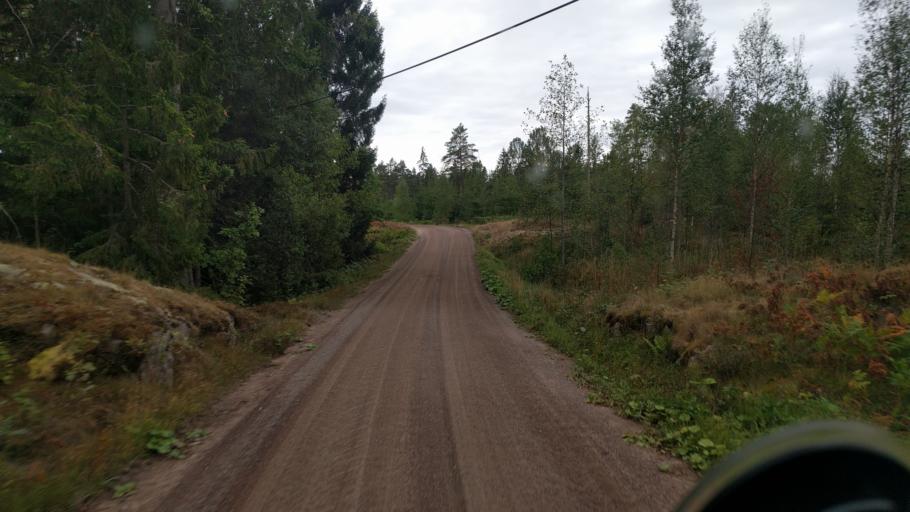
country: SE
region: Kalmar
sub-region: Vasterviks Kommun
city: Ankarsrum
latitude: 57.7553
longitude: 16.1819
